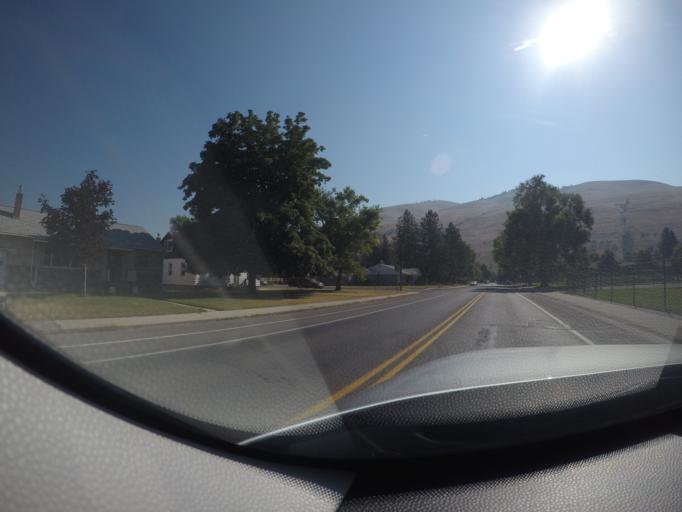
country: US
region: Montana
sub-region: Missoula County
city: Missoula
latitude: 46.8488
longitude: -113.9914
